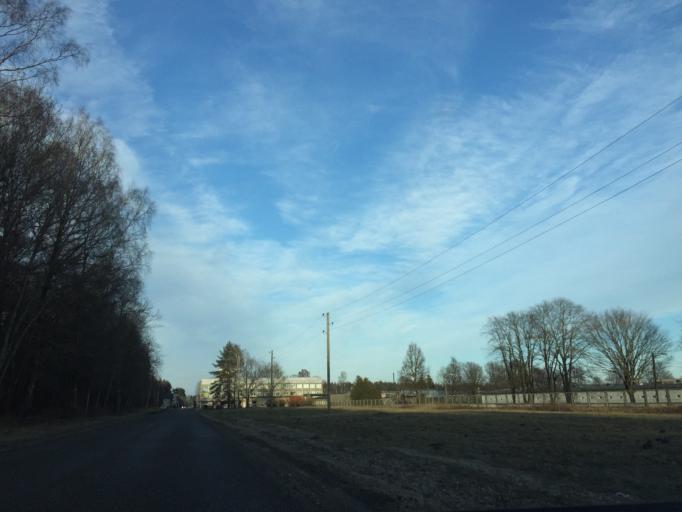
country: LV
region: Kekava
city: Kekava
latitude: 56.8273
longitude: 24.1944
